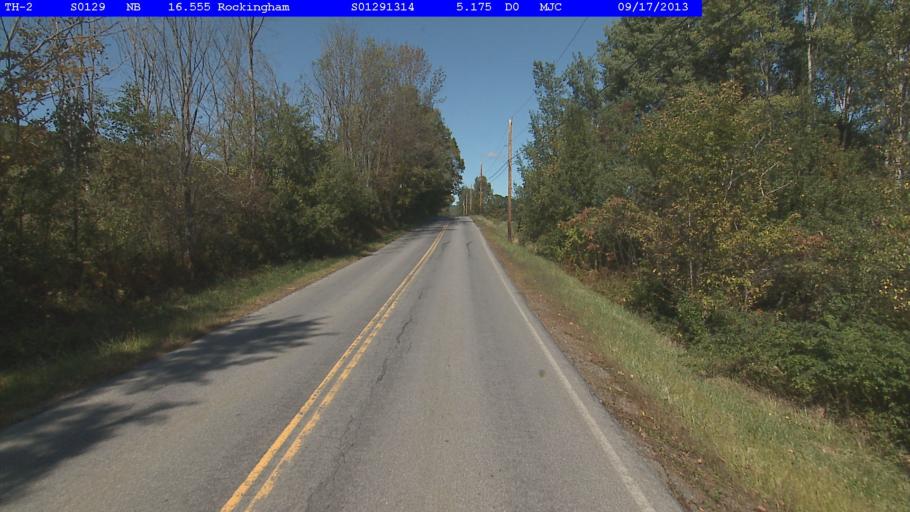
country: US
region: Vermont
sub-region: Windham County
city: Rockingham
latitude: 43.1909
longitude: -72.5116
